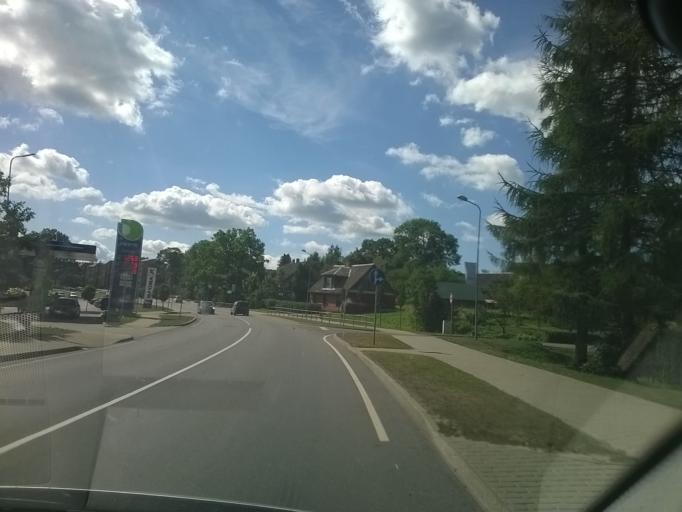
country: LV
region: Aluksnes Rajons
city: Aluksne
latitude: 57.4302
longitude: 27.0387
